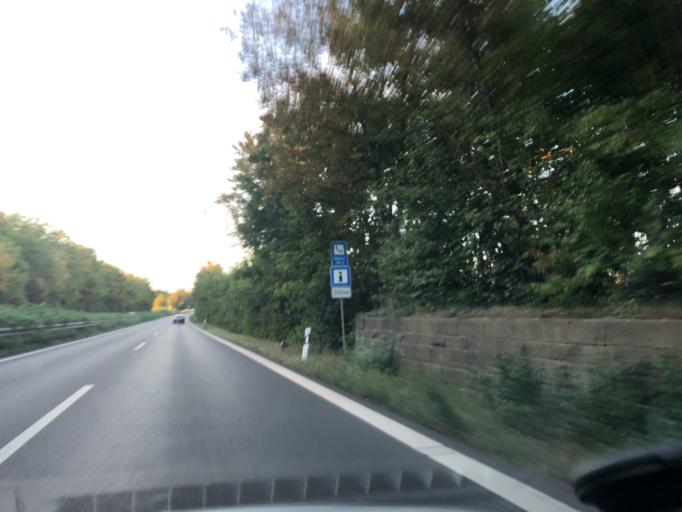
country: DE
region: Baden-Wuerttemberg
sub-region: Regierungsbezirk Stuttgart
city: Kornwestheim
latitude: 48.8681
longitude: 9.1973
